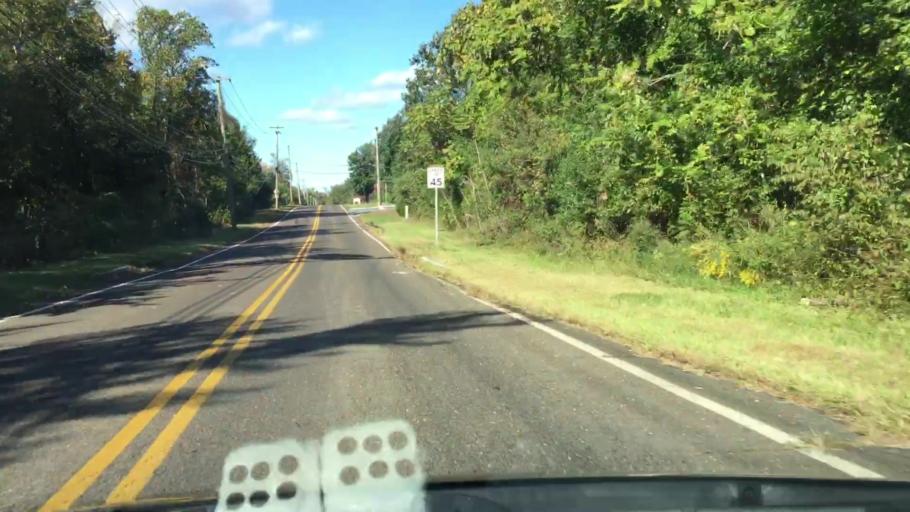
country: US
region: New Jersey
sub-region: Gloucester County
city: Turnersville
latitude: 39.7741
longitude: -75.0482
